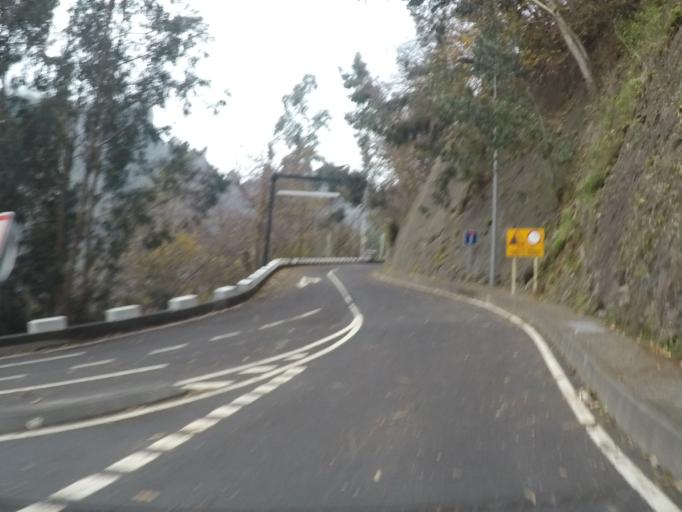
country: PT
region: Madeira
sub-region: Camara de Lobos
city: Curral das Freiras
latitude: 32.7249
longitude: -16.9632
